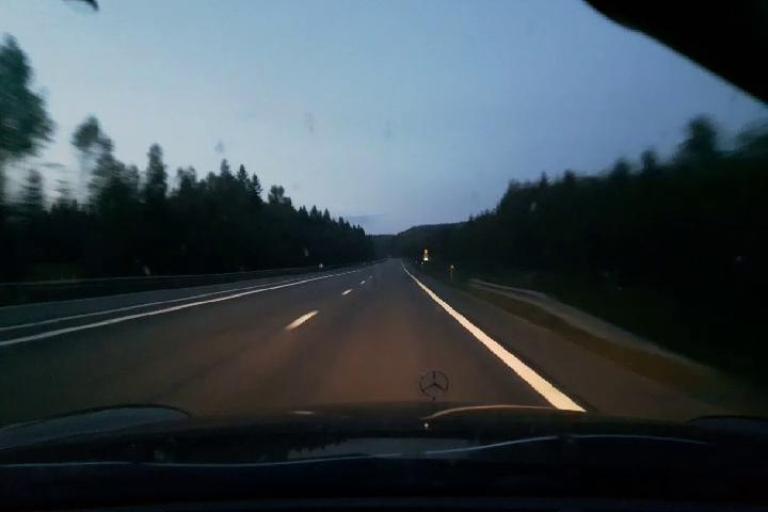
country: SE
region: Vaesternorrland
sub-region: Kramfors Kommun
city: Nordingra
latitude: 63.0761
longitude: 18.3627
